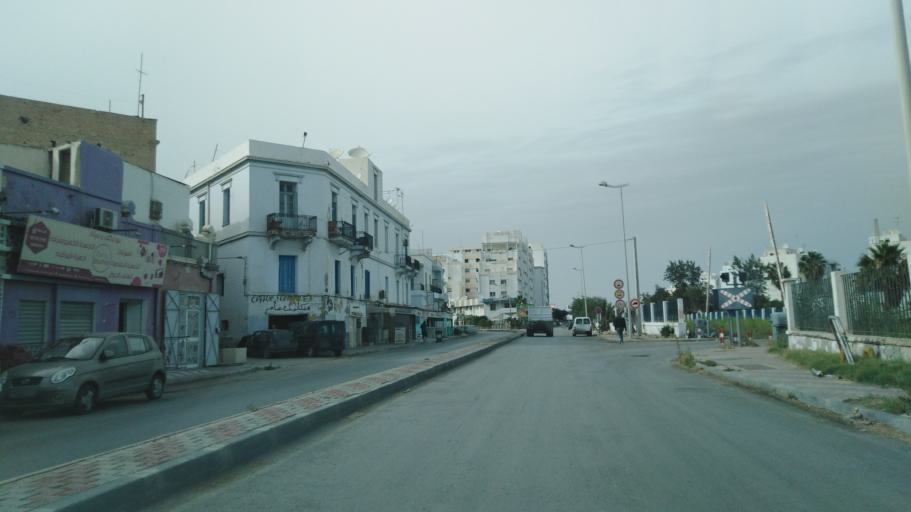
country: TN
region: Safaqis
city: Sfax
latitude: 34.7412
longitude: 10.7639
